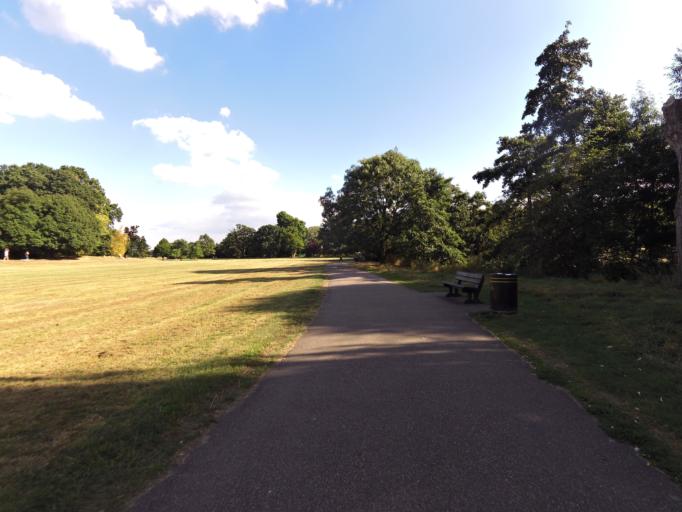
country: GB
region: England
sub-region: Greater London
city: Wood Green
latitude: 51.6194
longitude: -0.1330
